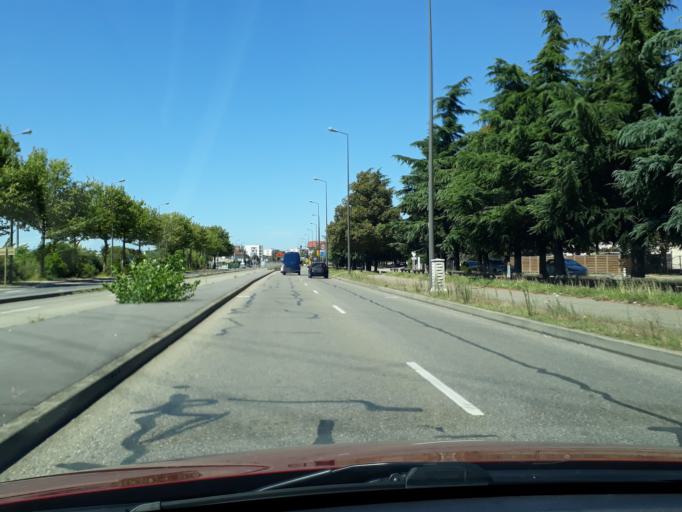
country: FR
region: Rhone-Alpes
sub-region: Departement du Rhone
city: Venissieux
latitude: 45.7153
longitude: 4.8952
